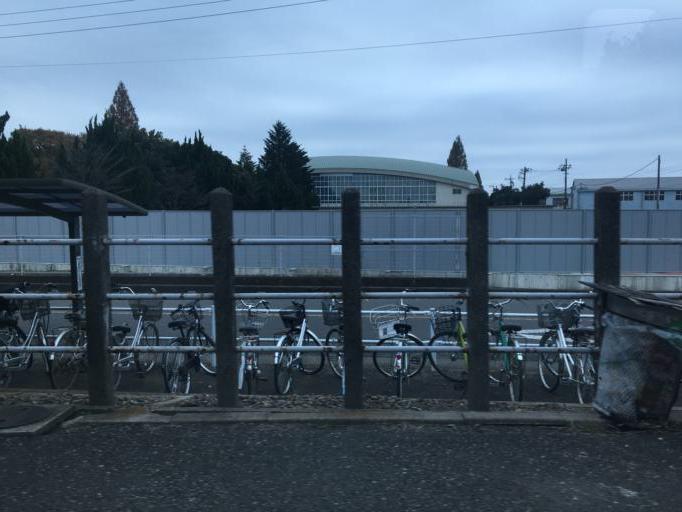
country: JP
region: Ibaraki
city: Yuki
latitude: 36.3007
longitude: 139.8538
